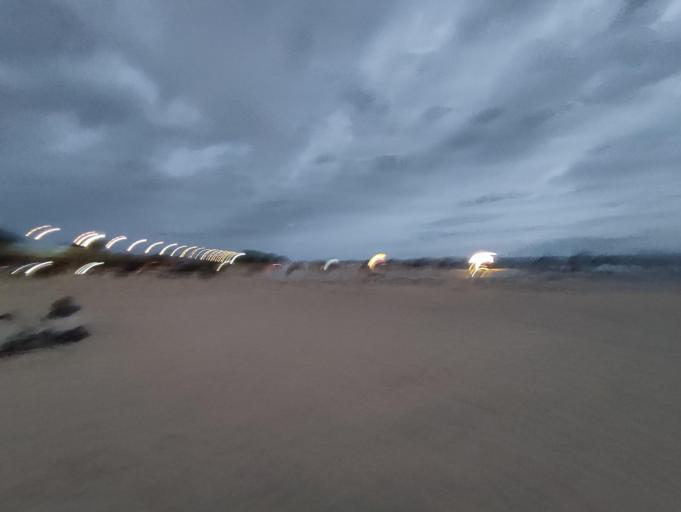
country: IN
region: Kerala
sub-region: Alappuzha
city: Alleppey
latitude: 9.4927
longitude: 76.3175
